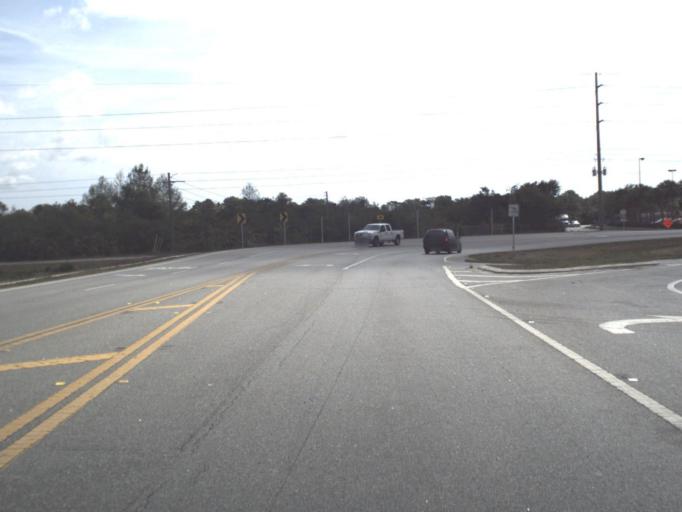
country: US
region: Florida
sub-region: Brevard County
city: Cocoa
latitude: 28.3971
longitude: -80.7564
